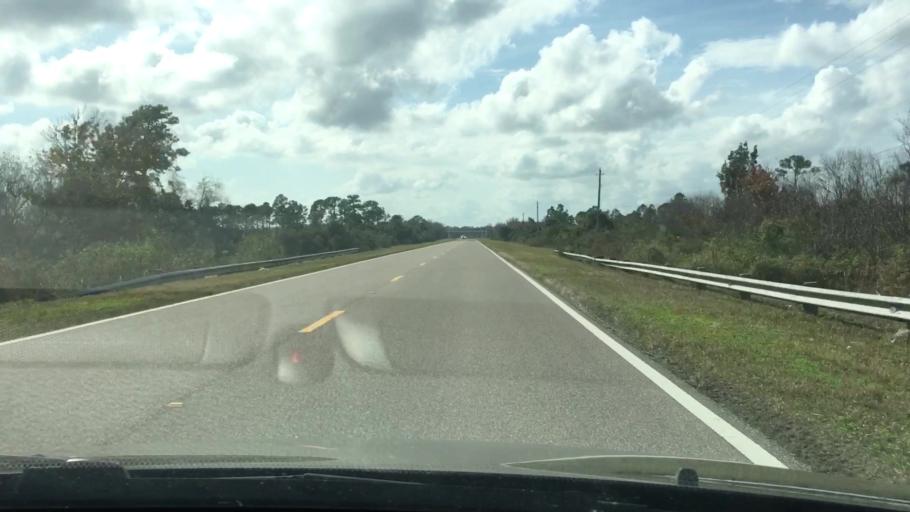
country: US
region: Florida
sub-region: Volusia County
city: Oak Hill
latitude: 28.7770
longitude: -80.8872
